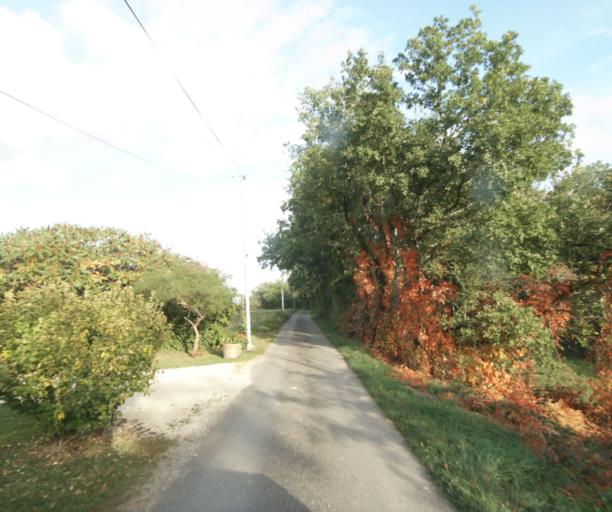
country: FR
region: Midi-Pyrenees
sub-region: Departement du Gers
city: Gondrin
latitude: 43.9025
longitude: 0.2764
